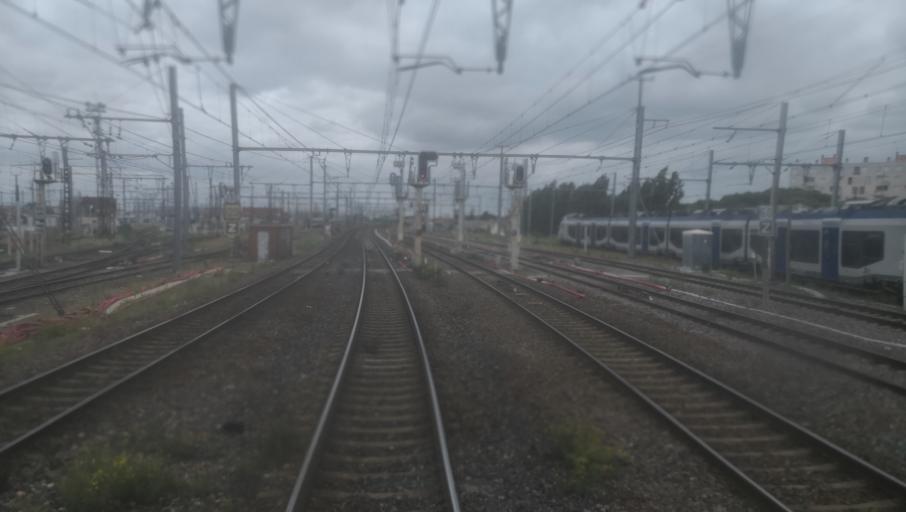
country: FR
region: Midi-Pyrenees
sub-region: Departement de la Haute-Garonne
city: Toulouse
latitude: 43.6172
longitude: 1.4522
